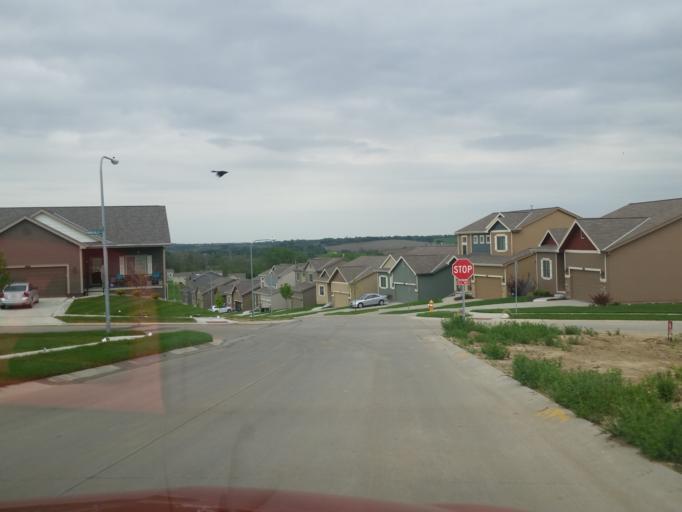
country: US
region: Nebraska
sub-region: Douglas County
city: Bennington
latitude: 41.3229
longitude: -96.1350
